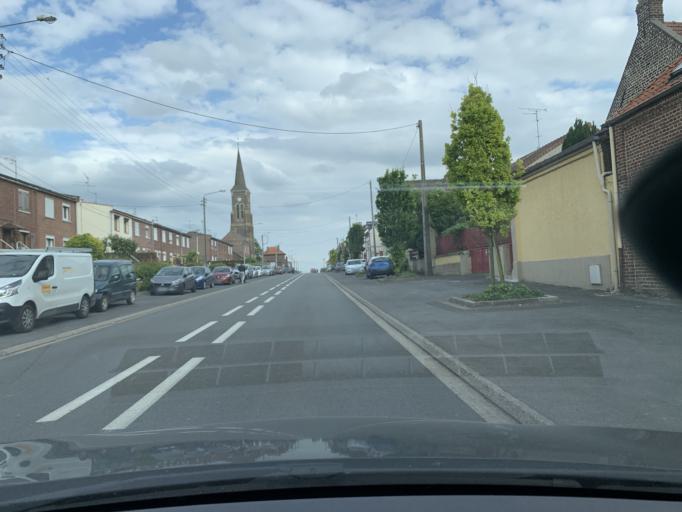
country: FR
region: Nord-Pas-de-Calais
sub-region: Departement du Nord
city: Proville
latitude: 50.1832
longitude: 3.1962
